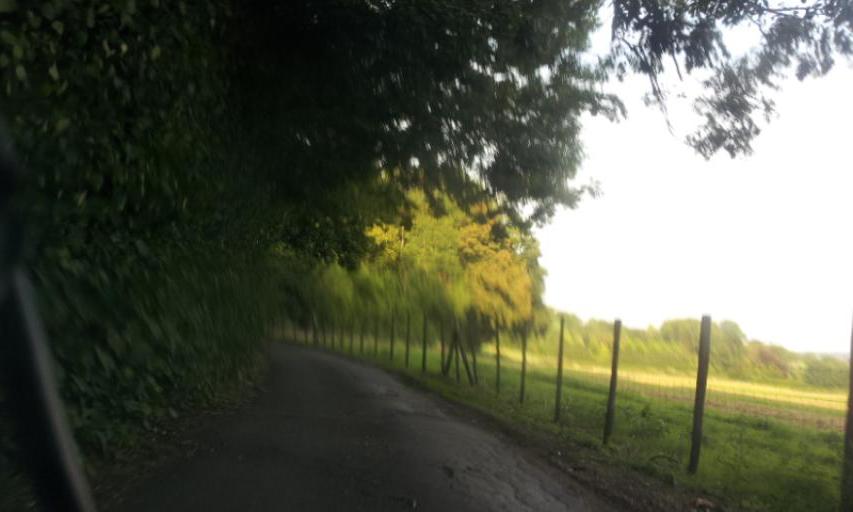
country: GB
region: England
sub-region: Kent
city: Wateringbury
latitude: 51.2660
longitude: 0.4536
